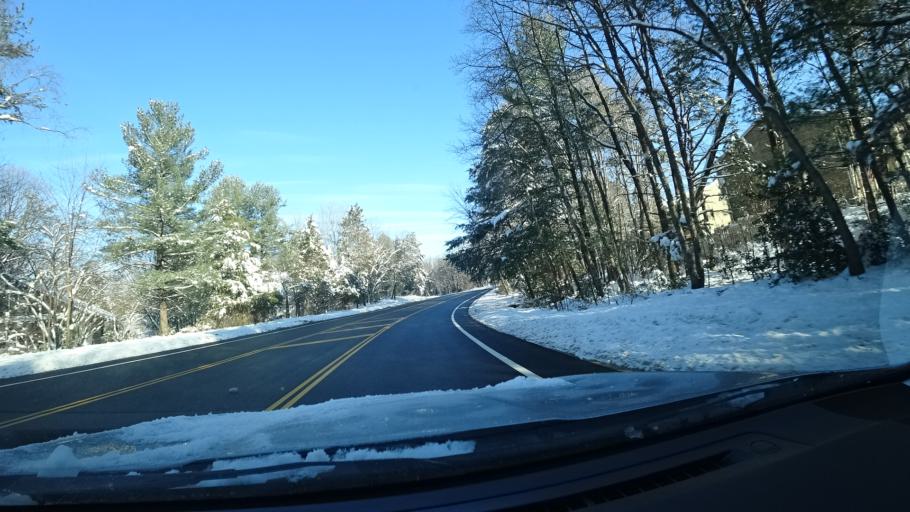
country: US
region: Virginia
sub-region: Fairfax County
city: Reston
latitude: 38.9709
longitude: -77.3577
